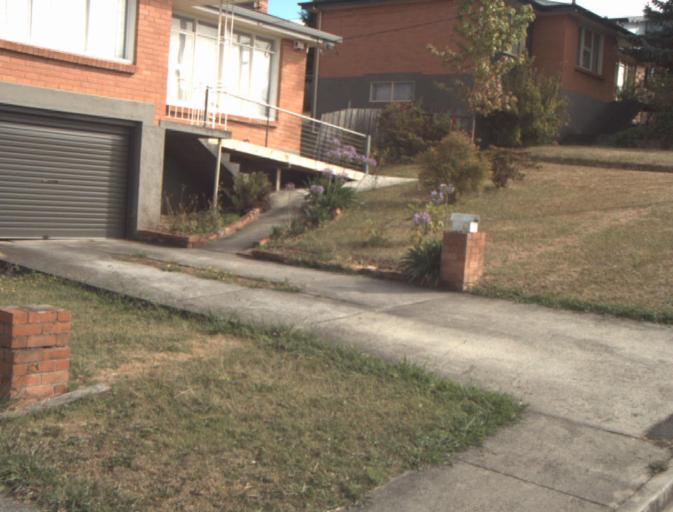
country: AU
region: Tasmania
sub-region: Launceston
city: Invermay
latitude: -41.3917
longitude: 147.1330
